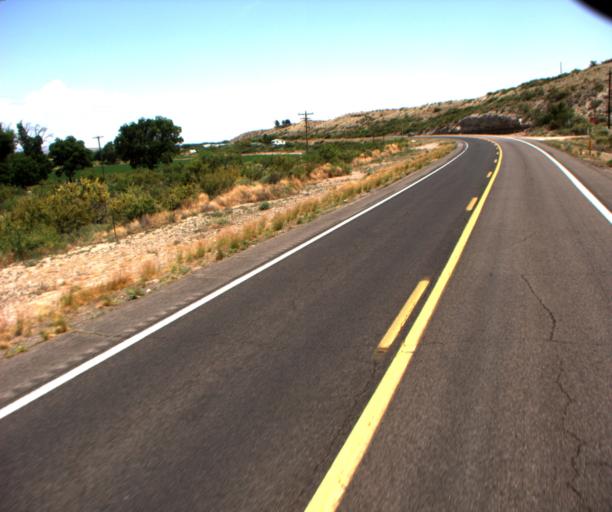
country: US
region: Arizona
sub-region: Greenlee County
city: Clifton
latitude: 32.7364
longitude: -109.1240
